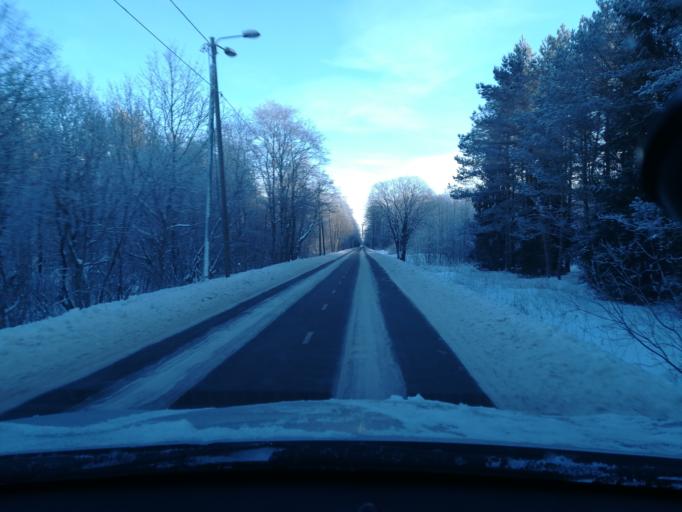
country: EE
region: Harju
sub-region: Saue vald
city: Laagri
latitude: 59.3908
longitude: 24.6121
